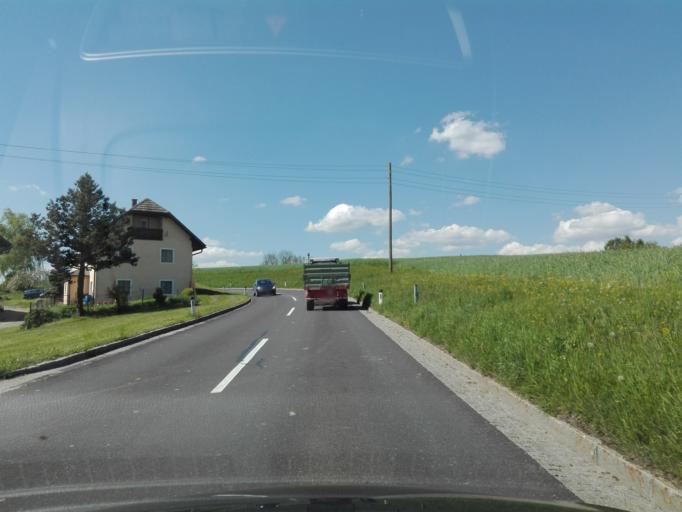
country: AT
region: Upper Austria
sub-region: Politischer Bezirk Urfahr-Umgebung
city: Feldkirchen an der Donau
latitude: 48.3510
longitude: 13.9439
